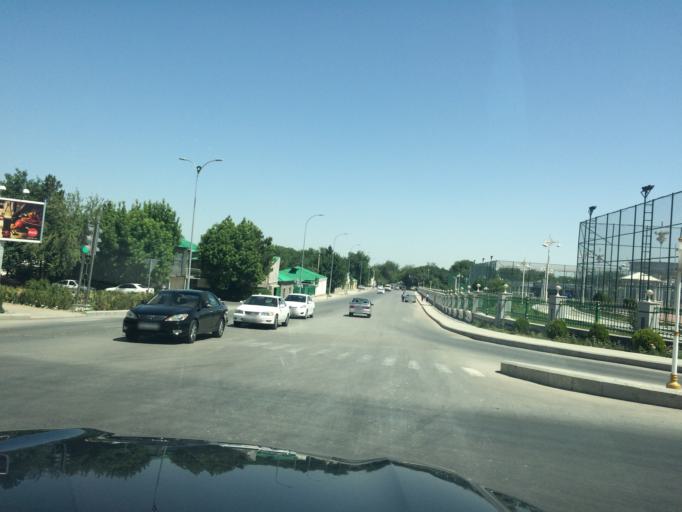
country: TM
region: Ahal
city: Ashgabat
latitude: 37.9432
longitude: 58.3603
